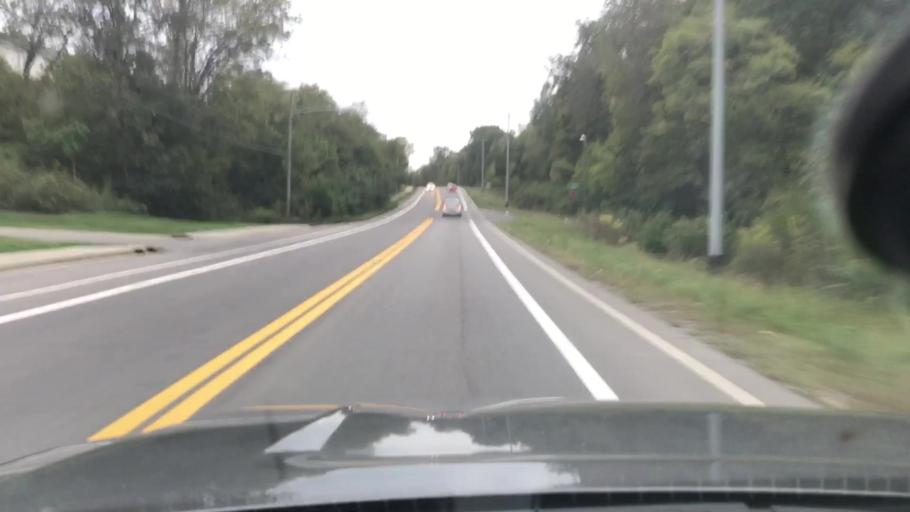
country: US
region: Tennessee
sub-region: Davidson County
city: Belle Meade
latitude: 36.1224
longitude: -86.9137
